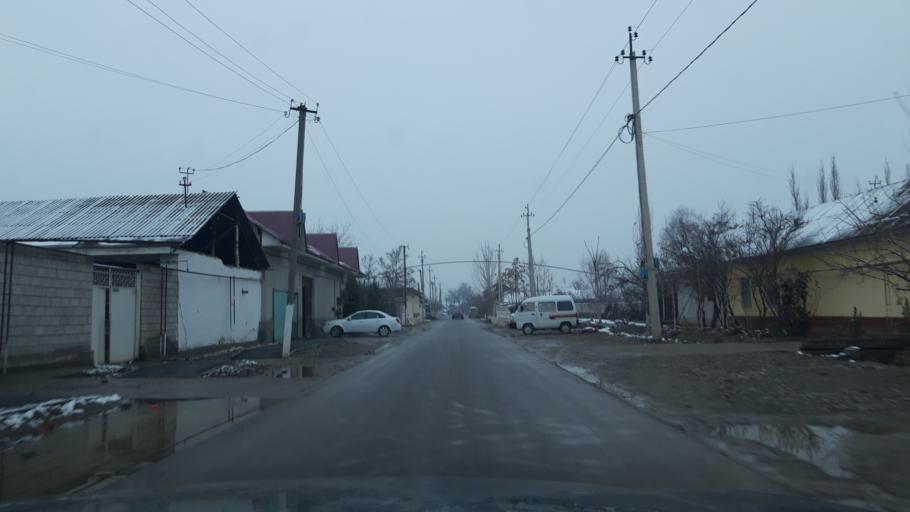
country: UZ
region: Andijon
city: Andijon
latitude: 40.7411
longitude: 72.2567
